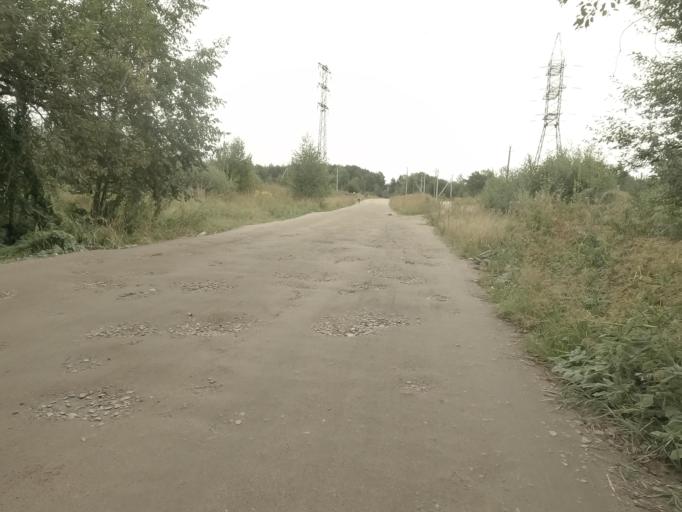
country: RU
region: Leningrad
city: Kirovsk
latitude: 59.8986
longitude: 31.0033
